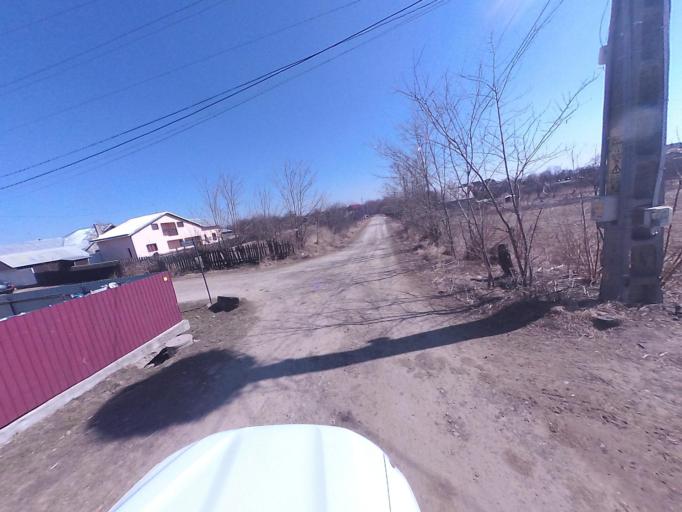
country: RO
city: Vanatori-Neamt
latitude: 47.1827
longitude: 26.3286
